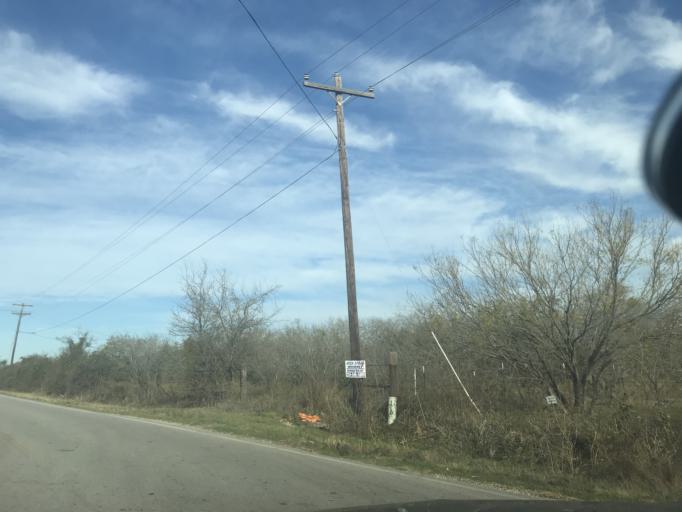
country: US
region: Texas
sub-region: Travis County
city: Manor
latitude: 30.2846
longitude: -97.5197
